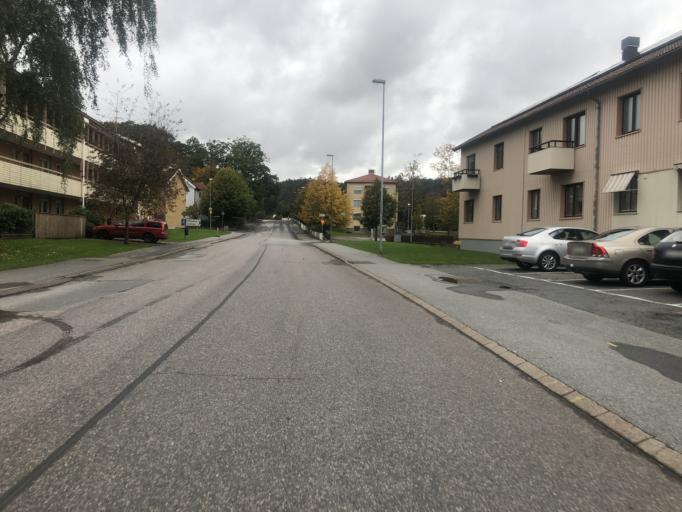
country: SE
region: Vaestra Goetaland
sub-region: Molndal
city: Moelndal
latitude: 57.6588
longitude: 12.0097
